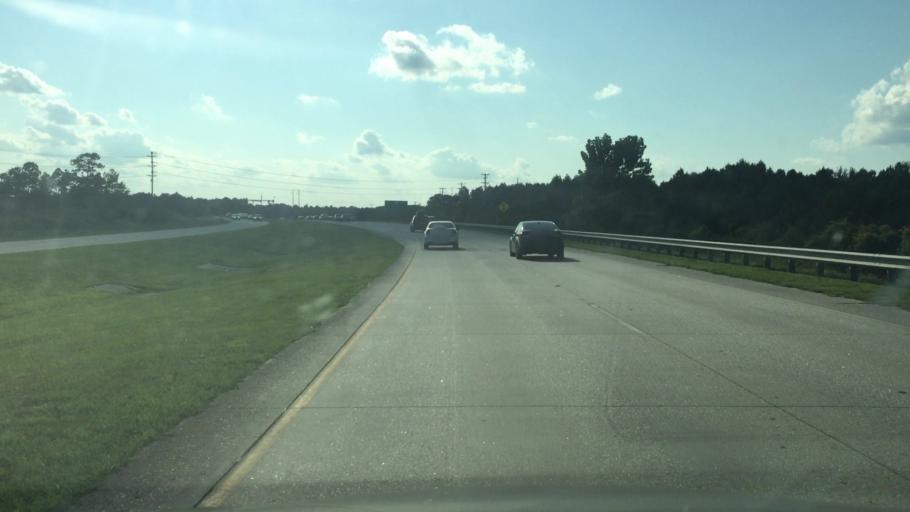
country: US
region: South Carolina
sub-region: Horry County
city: North Myrtle Beach
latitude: 33.8379
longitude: -78.6910
